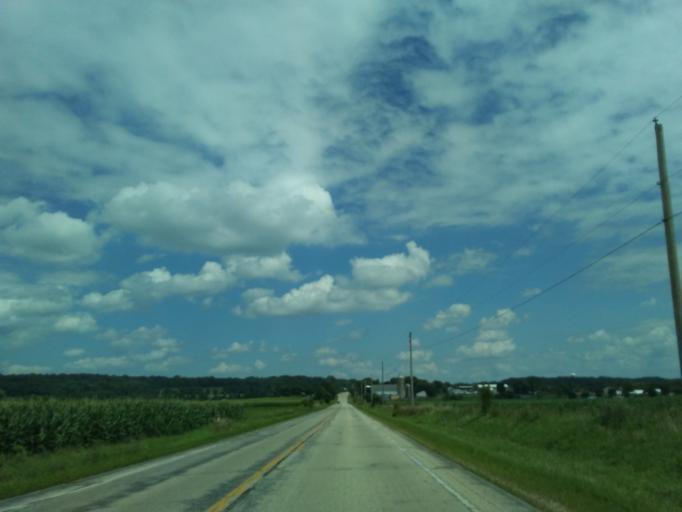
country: US
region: Wisconsin
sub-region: Dane County
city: Verona
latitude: 43.0130
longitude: -89.5718
